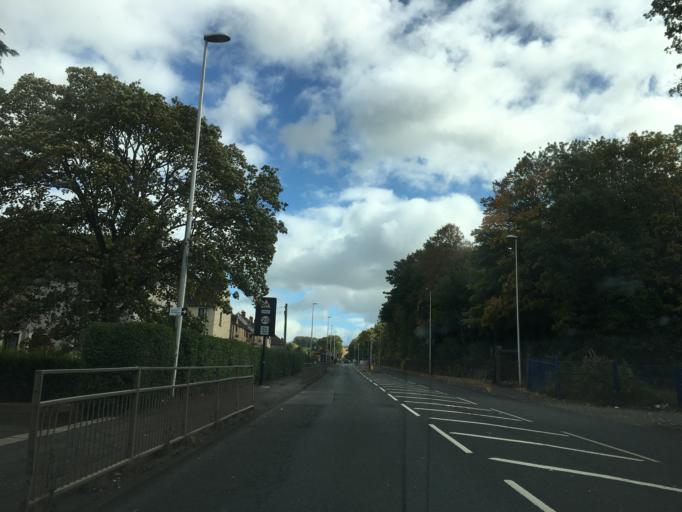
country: GB
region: Scotland
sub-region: Midlothian
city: Dalkeith
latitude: 55.8904
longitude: -3.0556
